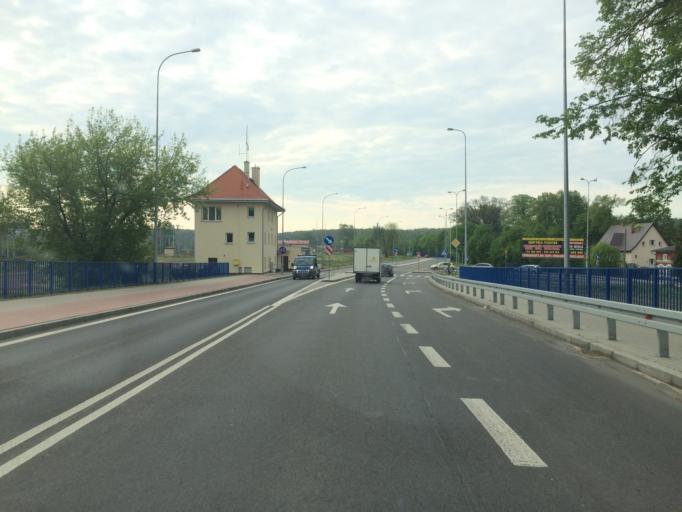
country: PL
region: Warmian-Masurian Voivodeship
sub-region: Powiat dzialdowski
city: Ilowo -Osada
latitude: 53.1645
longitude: 20.2946
